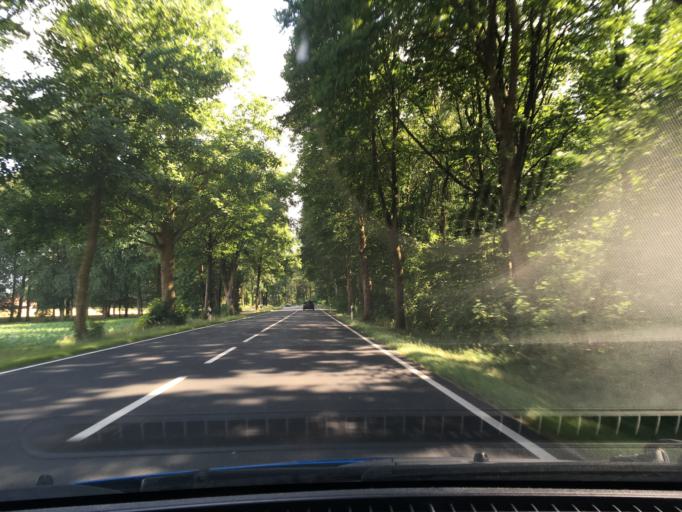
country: DE
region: Lower Saxony
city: Welle
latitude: 53.2274
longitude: 9.8063
